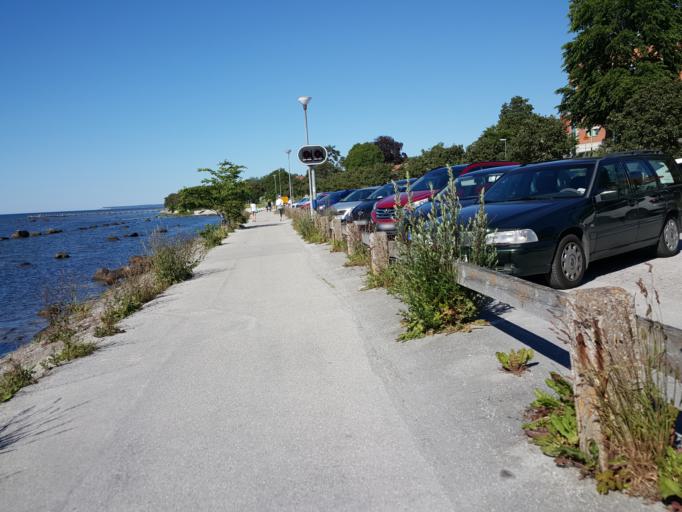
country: SE
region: Gotland
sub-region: Gotland
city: Visby
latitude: 57.6493
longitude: 18.2989
